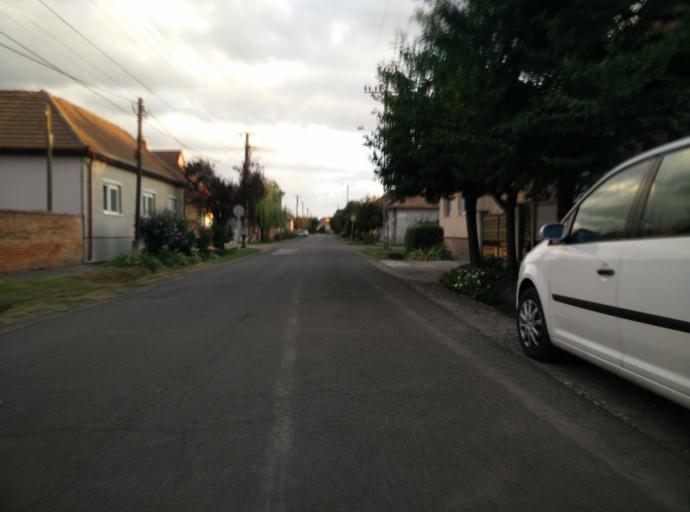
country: HU
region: Heves
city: Hatvan
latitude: 47.6641
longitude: 19.7008
